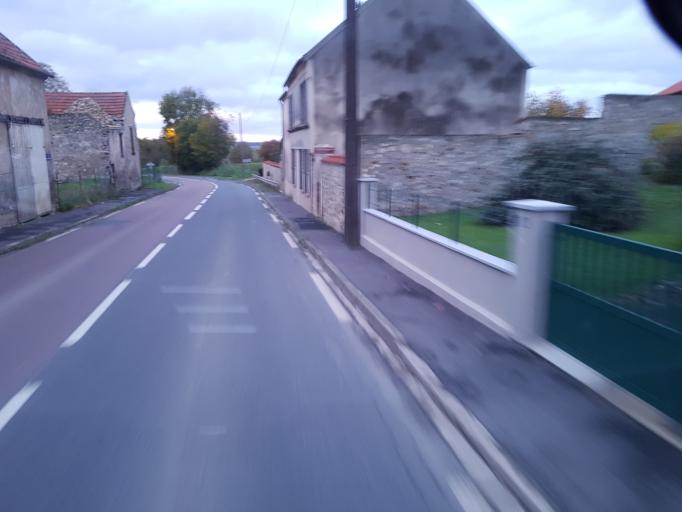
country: FR
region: Picardie
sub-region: Departement de l'Aisne
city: Coincy
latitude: 49.1541
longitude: 3.3869
